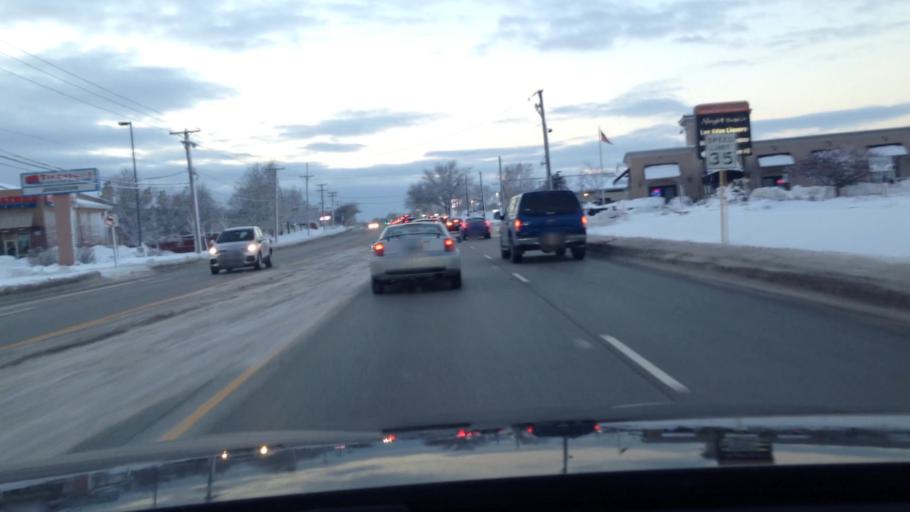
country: US
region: Illinois
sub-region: Lake County
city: Kildeer
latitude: 42.1450
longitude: -88.0281
